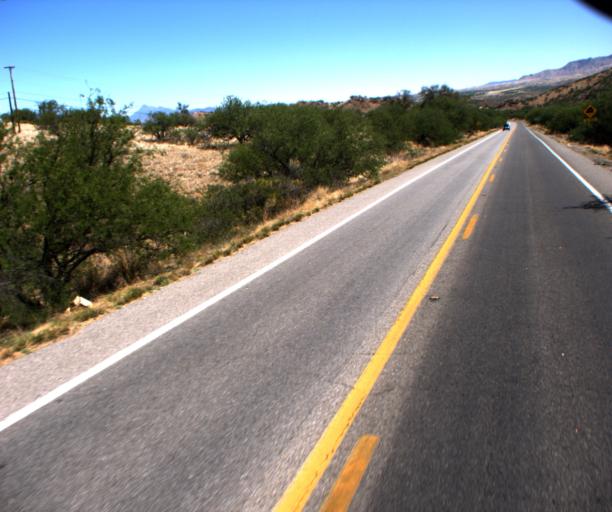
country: US
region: Arizona
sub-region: Santa Cruz County
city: Nogales
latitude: 31.3737
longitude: -110.8898
